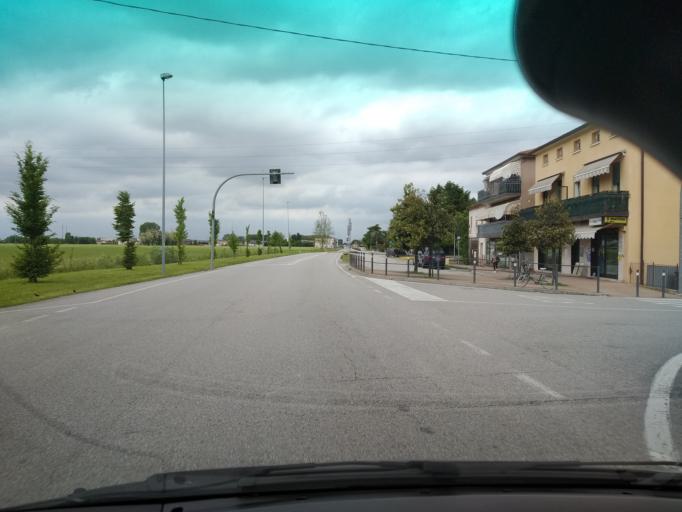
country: IT
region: Veneto
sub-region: Provincia di Padova
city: Tremignon
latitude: 45.5194
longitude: 11.8033
